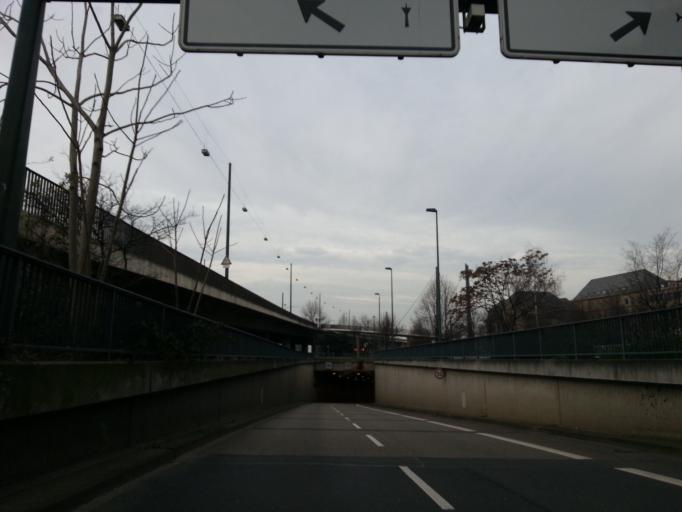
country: DE
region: North Rhine-Westphalia
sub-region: Regierungsbezirk Dusseldorf
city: Dusseldorf
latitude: 51.2179
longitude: 6.7689
